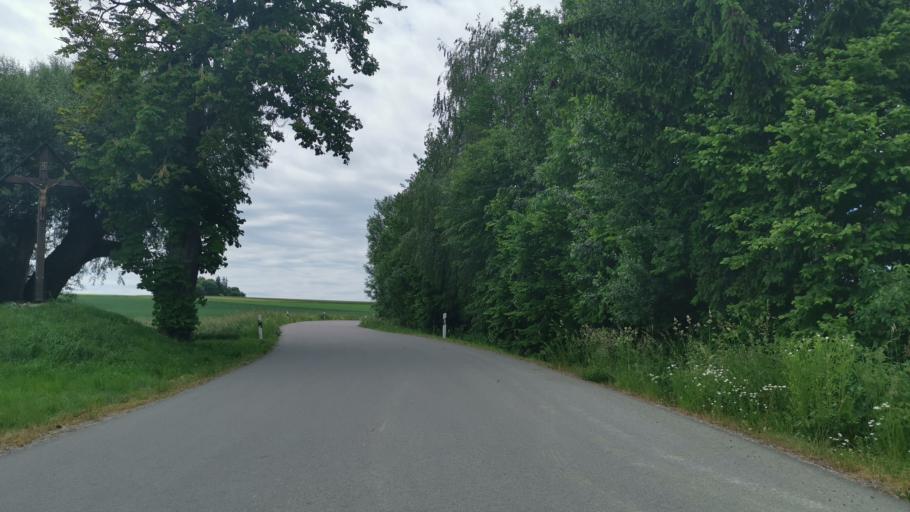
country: DE
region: Bavaria
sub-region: Upper Bavaria
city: Althegnenberg
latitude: 48.2417
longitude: 11.0398
